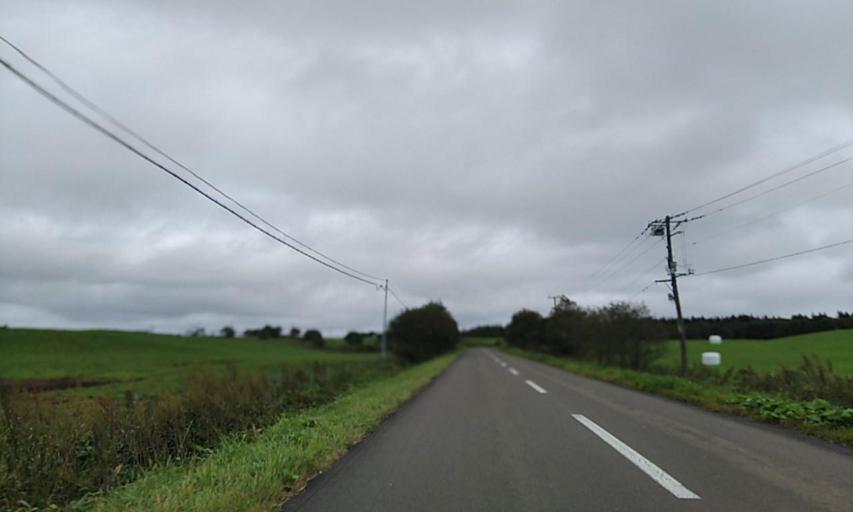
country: JP
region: Hokkaido
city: Nemuro
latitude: 43.2640
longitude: 145.2638
